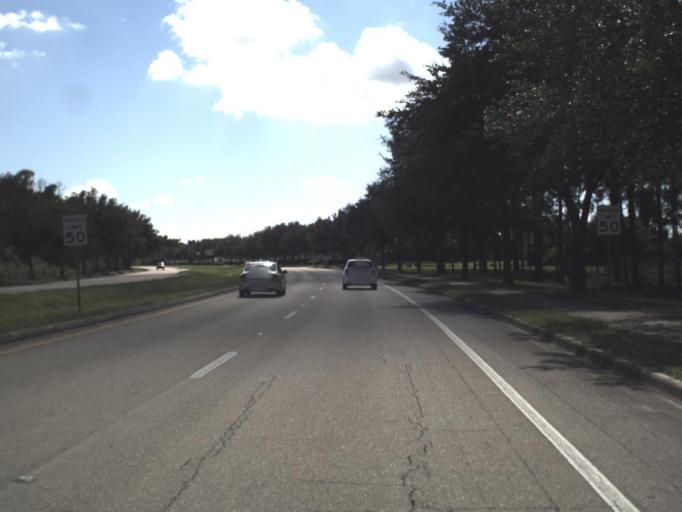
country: US
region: Florida
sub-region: Lee County
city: Palmona Park
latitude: 26.7128
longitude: -81.9388
